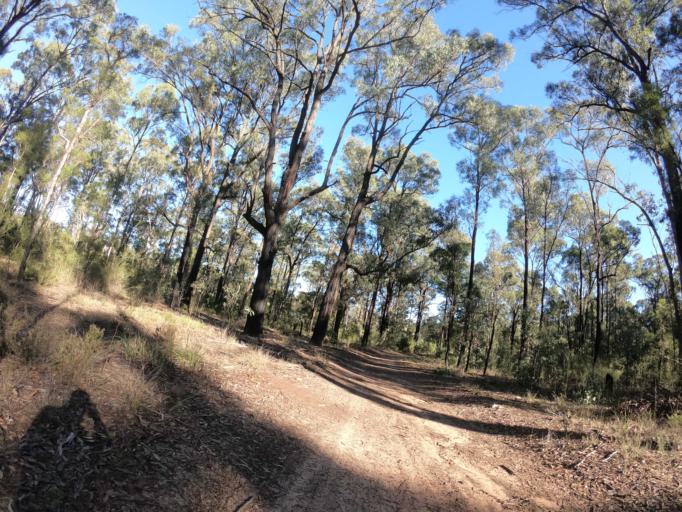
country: AU
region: New South Wales
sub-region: Hawkesbury
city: South Windsor
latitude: -33.6480
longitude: 150.7927
